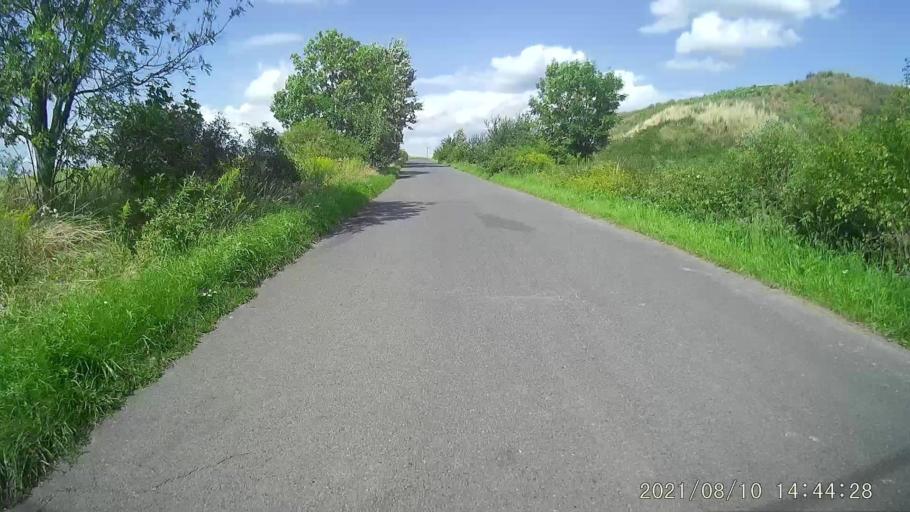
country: PL
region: Lower Silesian Voivodeship
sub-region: Powiat klodzki
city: Radkow
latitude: 50.5410
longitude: 16.4235
